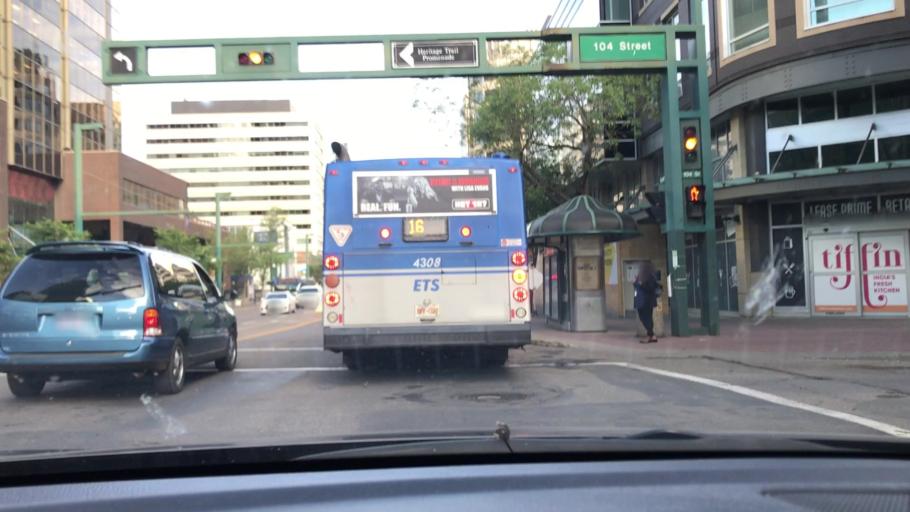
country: CA
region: Alberta
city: Edmonton
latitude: 53.5410
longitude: -113.4992
